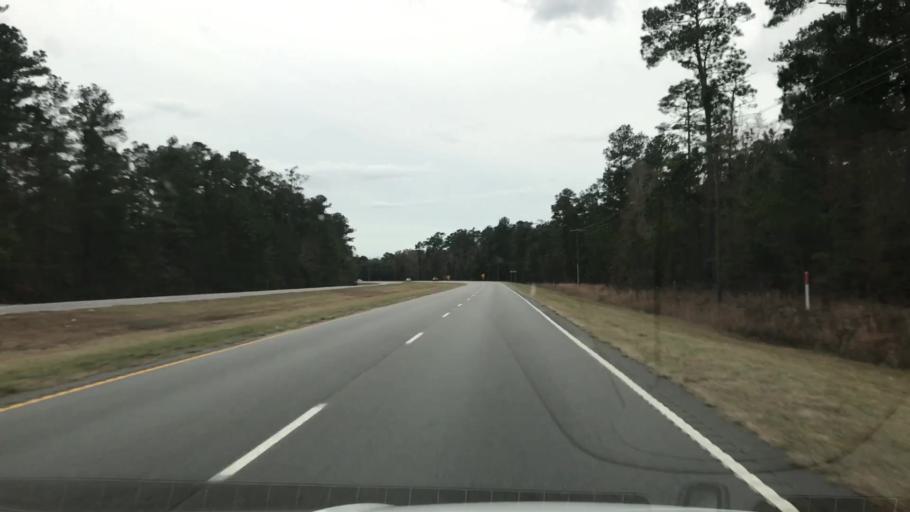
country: US
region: South Carolina
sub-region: Georgetown County
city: Georgetown
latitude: 33.2549
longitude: -79.3721
